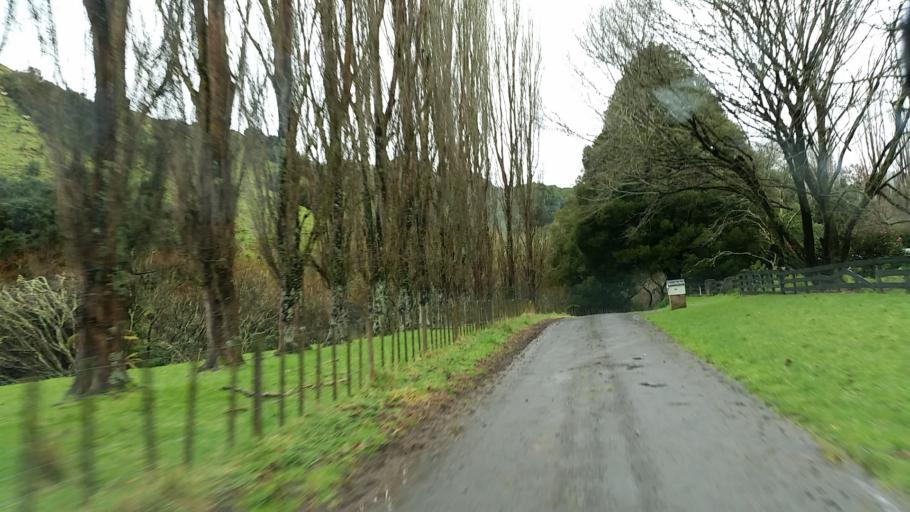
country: NZ
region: Taranaki
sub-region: South Taranaki District
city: Eltham
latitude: -39.5021
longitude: 174.4219
